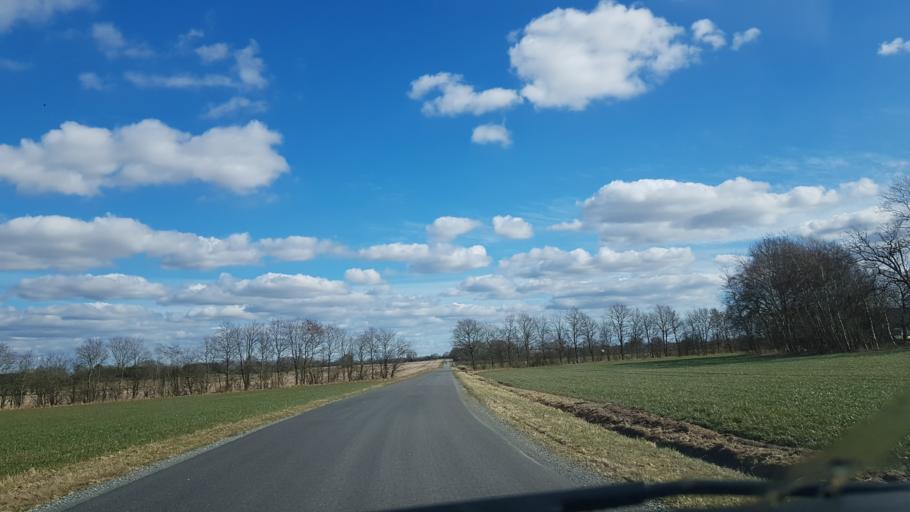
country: DK
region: South Denmark
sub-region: Kolding Kommune
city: Vamdrup
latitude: 55.4102
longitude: 9.2181
